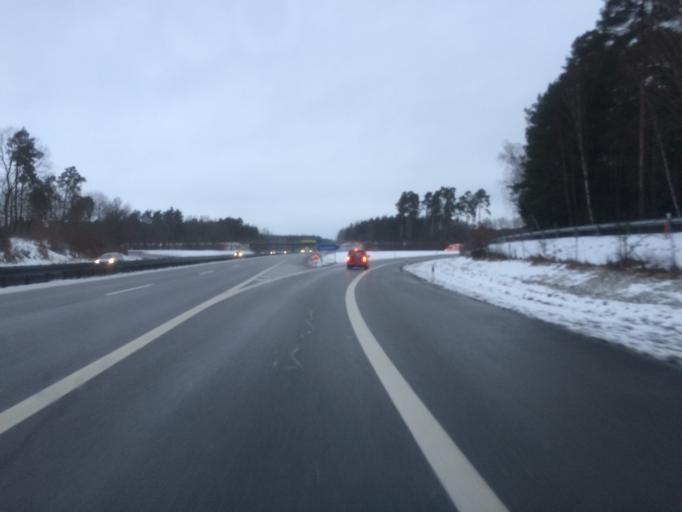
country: DE
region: Bavaria
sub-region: Upper Palatinate
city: Wackersdorf
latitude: 49.3404
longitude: 12.1501
